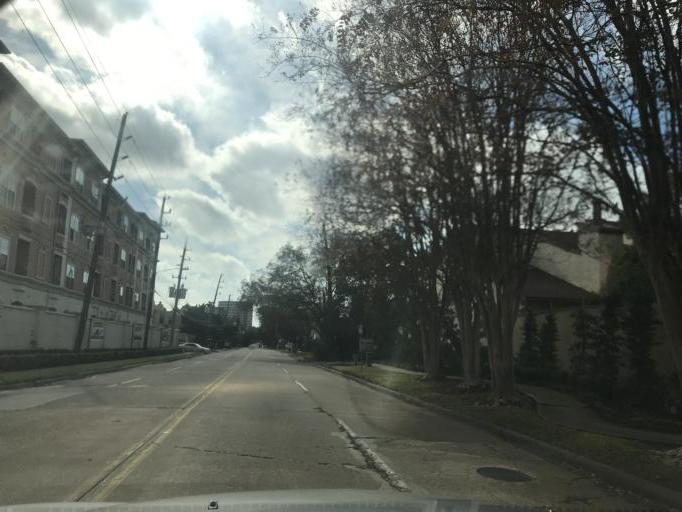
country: US
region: Texas
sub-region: Harris County
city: Hunters Creek Village
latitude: 29.7473
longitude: -95.4827
